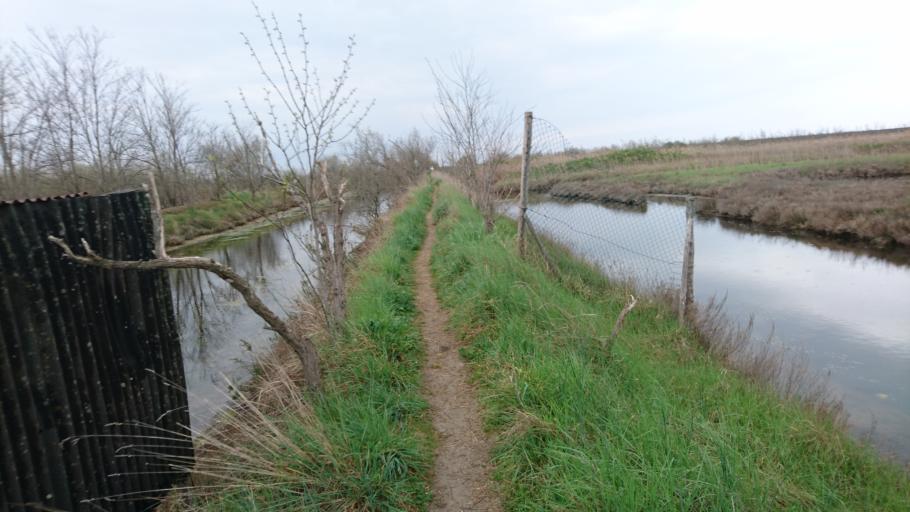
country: IT
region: Veneto
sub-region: Provincia di Venezia
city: Ca' Savio
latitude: 45.4908
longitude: 12.4894
